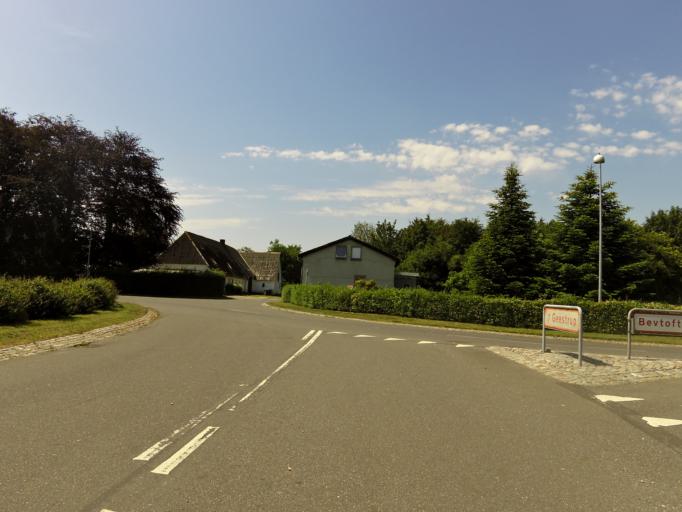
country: DK
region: South Denmark
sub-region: Haderslev Kommune
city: Vojens
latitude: 55.1579
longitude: 9.2163
